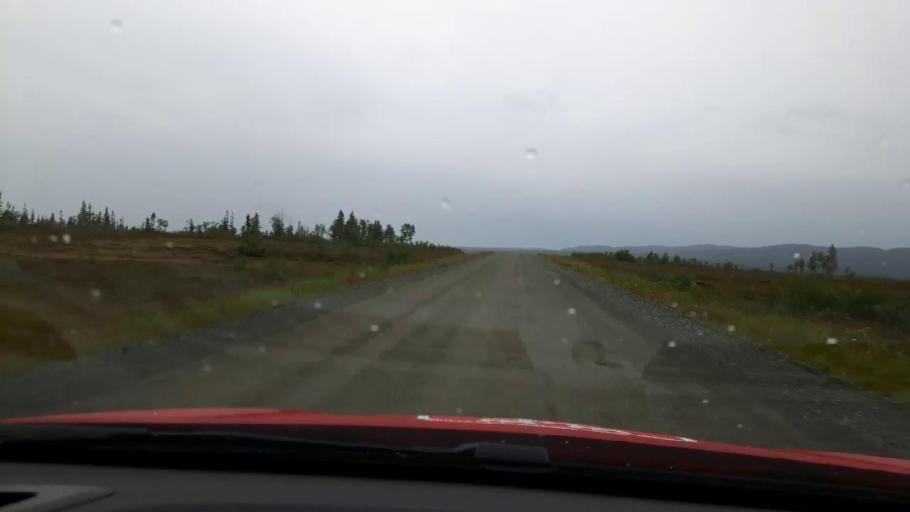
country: NO
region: Nord-Trondelag
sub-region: Meraker
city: Meraker
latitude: 63.5898
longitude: 12.2694
